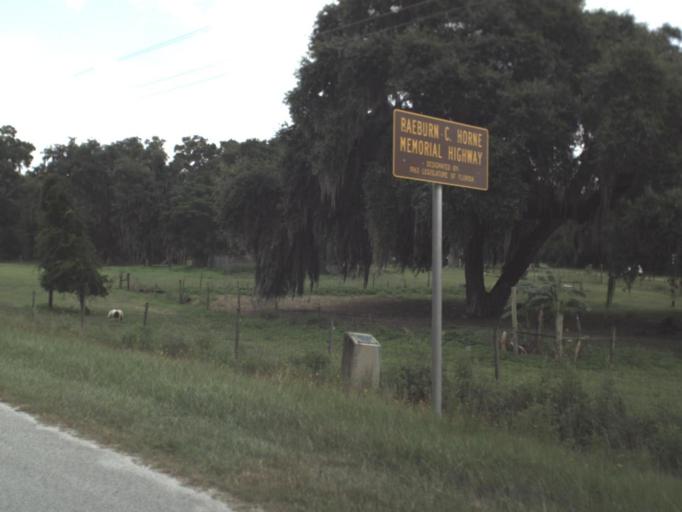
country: US
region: Florida
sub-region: Madison County
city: Madison
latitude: 30.4696
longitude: -83.3744
